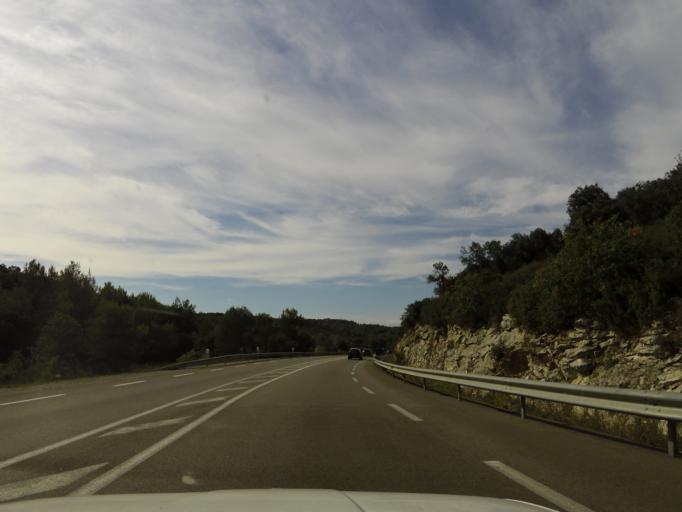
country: FR
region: Languedoc-Roussillon
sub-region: Departement du Gard
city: La Calmette
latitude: 43.8892
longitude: 4.2939
